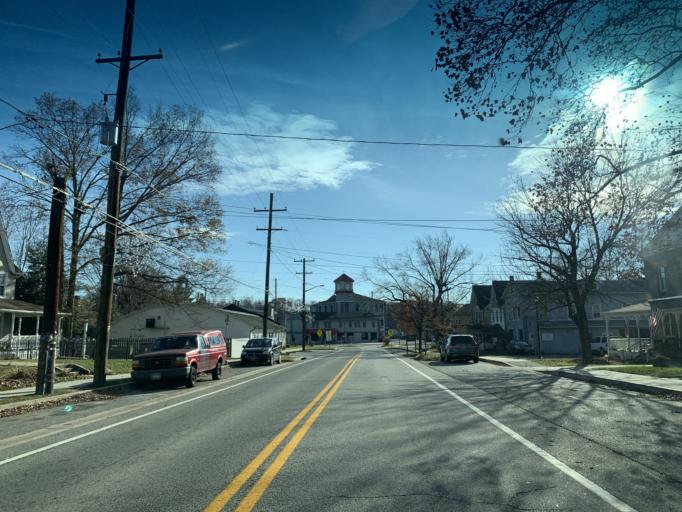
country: US
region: Maryland
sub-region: Cecil County
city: Perryville
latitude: 39.5612
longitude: -76.0713
